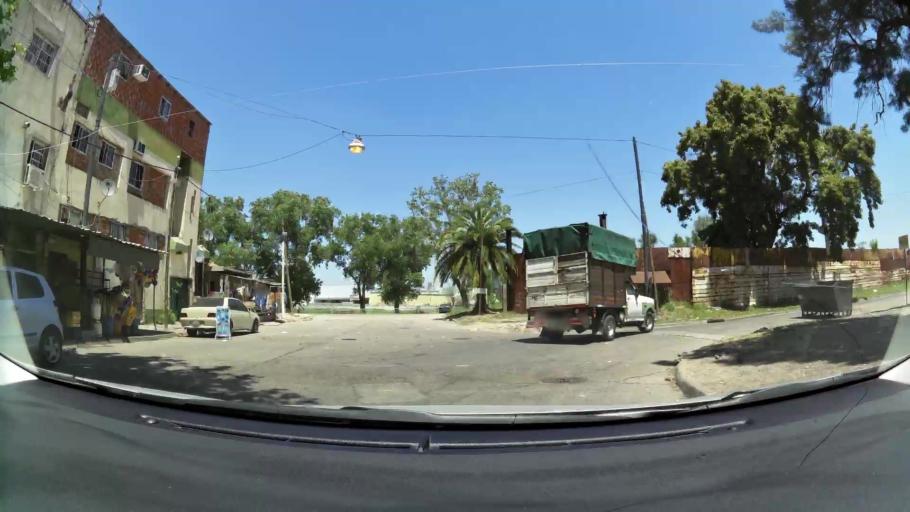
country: AR
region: Buenos Aires
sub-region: Partido de Avellaneda
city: Avellaneda
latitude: -34.6608
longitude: -58.3916
